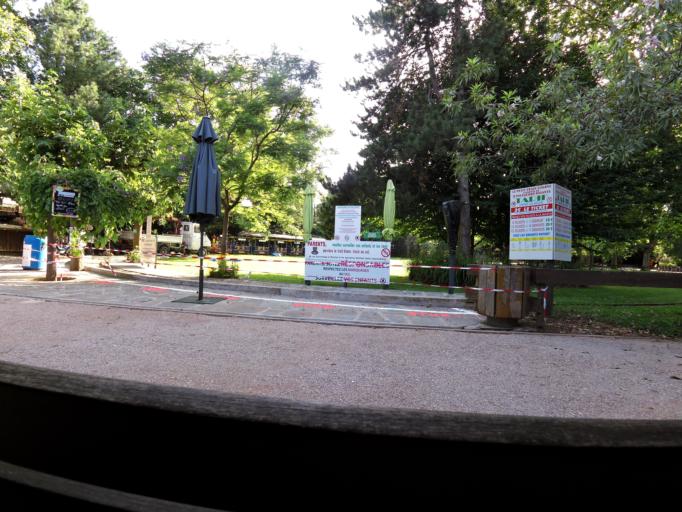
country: FR
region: Provence-Alpes-Cote d'Azur
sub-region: Departement du Var
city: Hyeres
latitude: 43.1099
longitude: 6.1367
